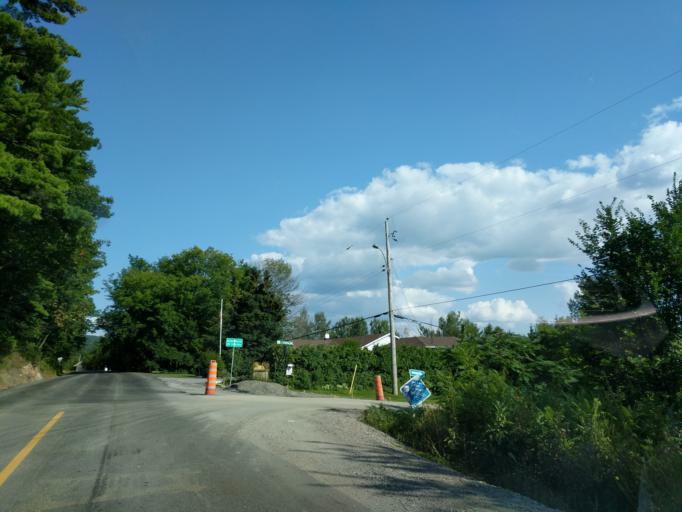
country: CA
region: Quebec
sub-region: Outaouais
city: Wakefield
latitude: 45.4953
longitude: -75.9107
